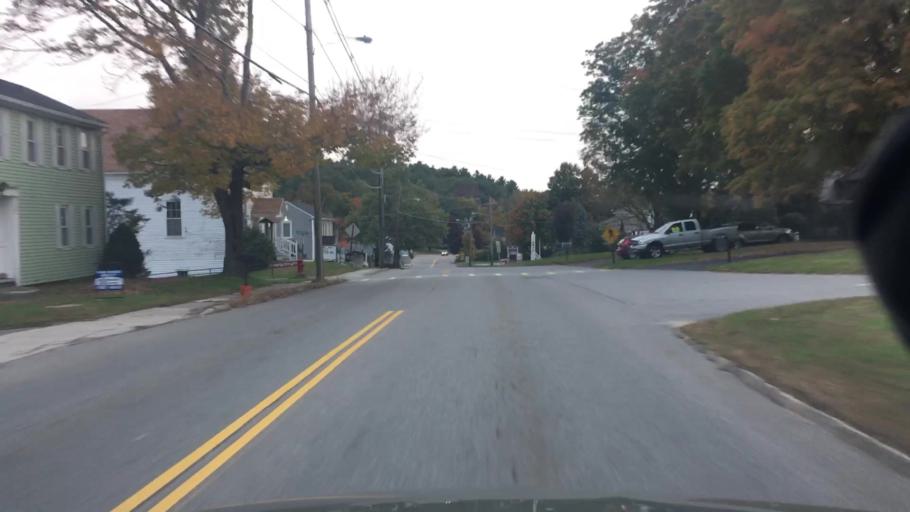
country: US
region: Massachusetts
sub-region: Worcester County
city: Charlton
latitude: 42.1356
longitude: -71.9698
